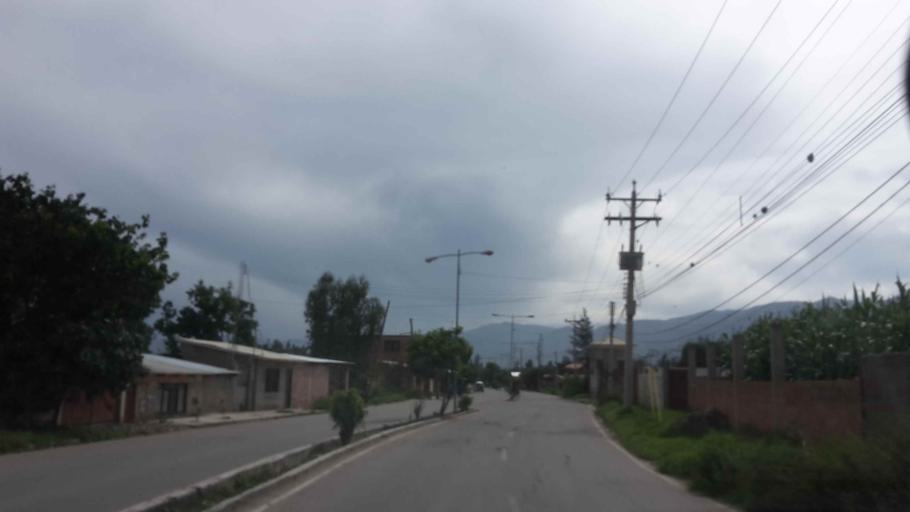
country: BO
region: Cochabamba
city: Cochabamba
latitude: -17.3324
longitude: -66.2507
